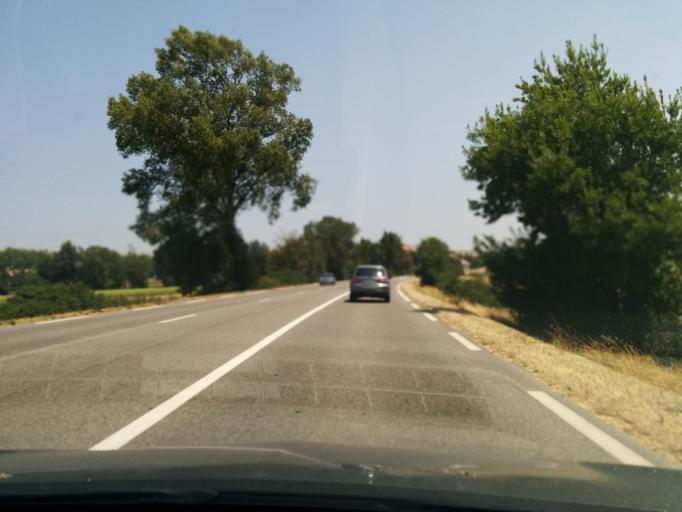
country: FR
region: Midi-Pyrenees
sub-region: Departement de la Haute-Garonne
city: Baziege
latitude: 43.4505
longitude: 1.6167
